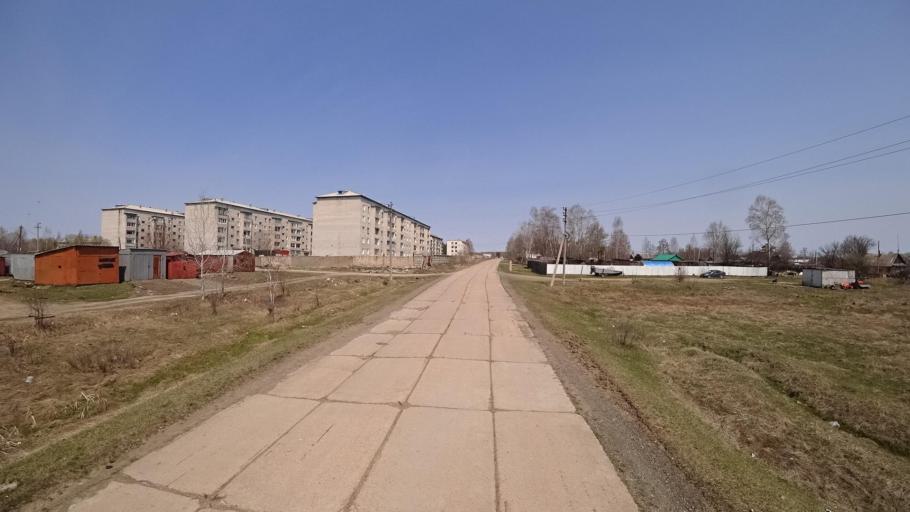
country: RU
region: Khabarovsk Krai
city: Selikhino
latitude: 50.3868
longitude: 137.3734
